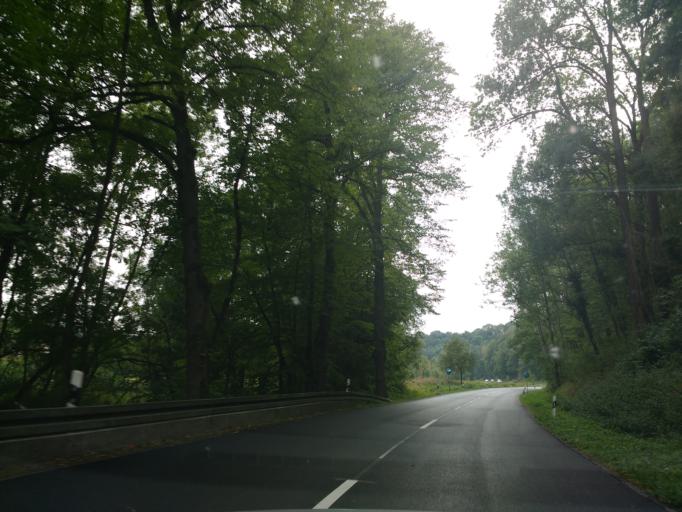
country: DE
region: North Rhine-Westphalia
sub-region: Regierungsbezirk Detmold
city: Paderborn
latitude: 51.6534
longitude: 8.7254
